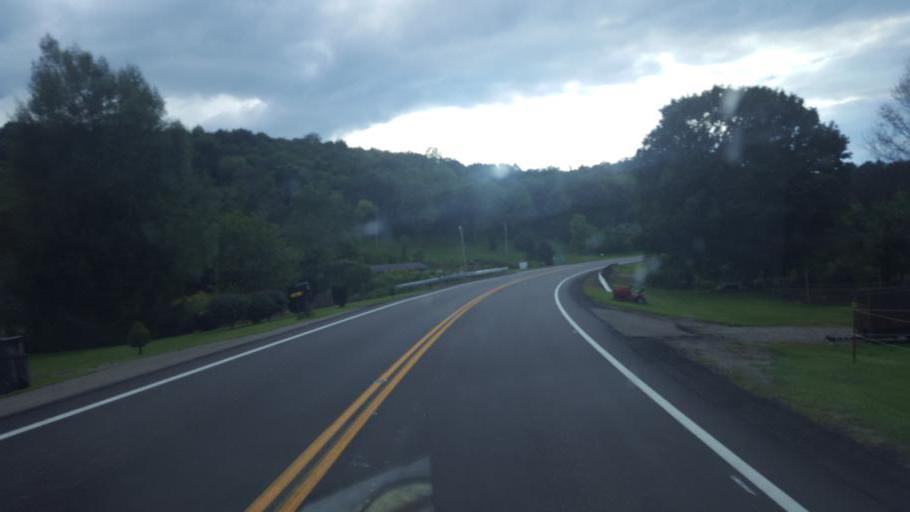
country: US
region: Ohio
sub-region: Knox County
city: Oak Hill
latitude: 40.4579
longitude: -82.1705
